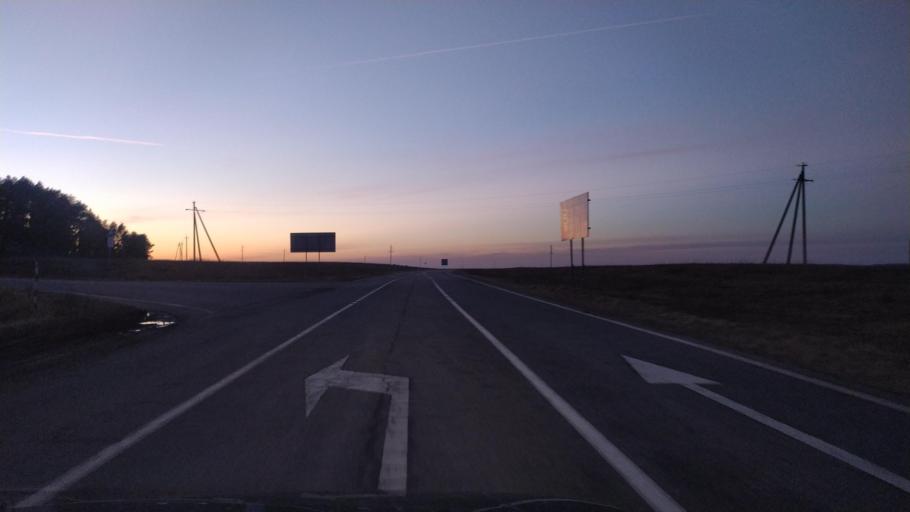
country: BY
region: Brest
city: Kamyanyets
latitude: 52.4030
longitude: 23.8670
